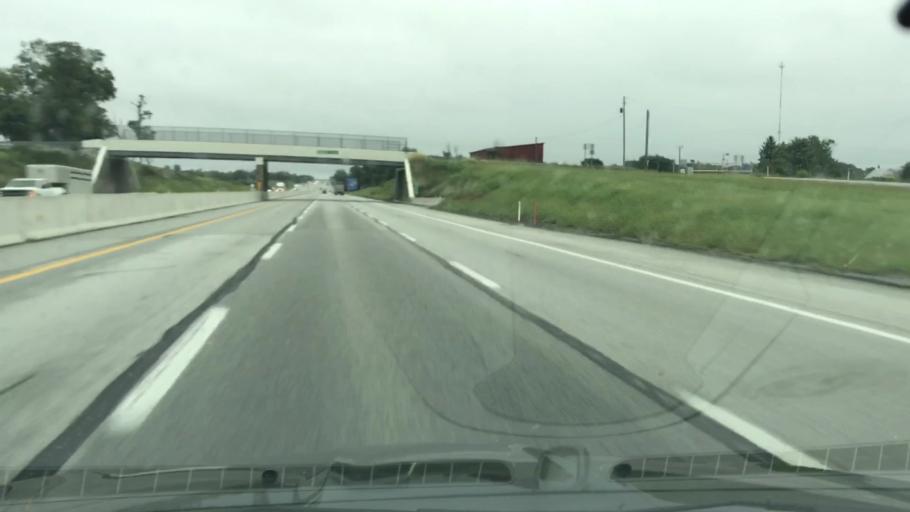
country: US
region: Pennsylvania
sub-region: Cumberland County
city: Newville
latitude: 40.2048
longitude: -77.3146
